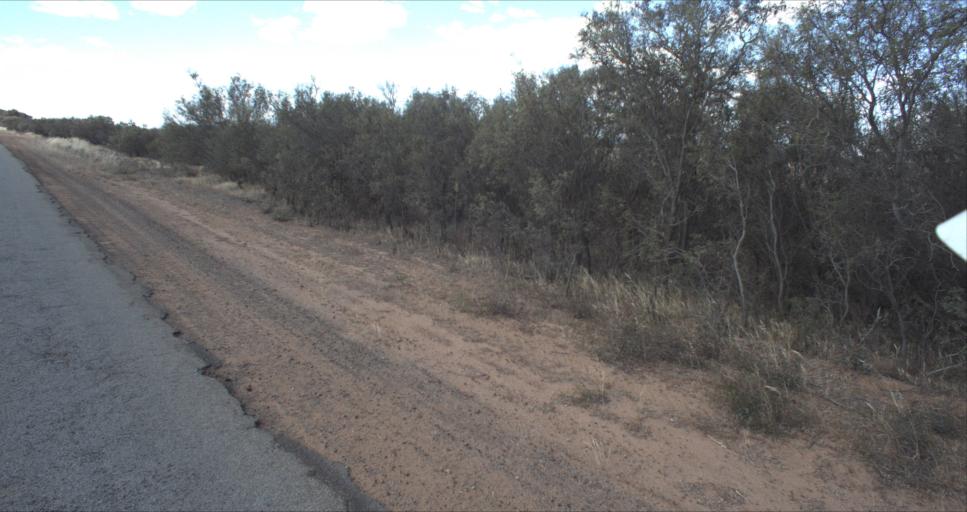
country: AU
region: New South Wales
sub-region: Leeton
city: Leeton
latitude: -34.4805
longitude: 146.2492
